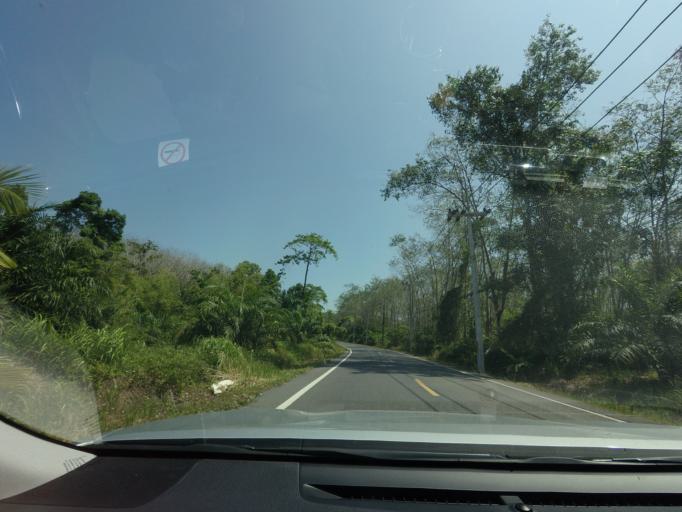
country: TH
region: Phangnga
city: Takua Thung
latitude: 8.2535
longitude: 98.4204
